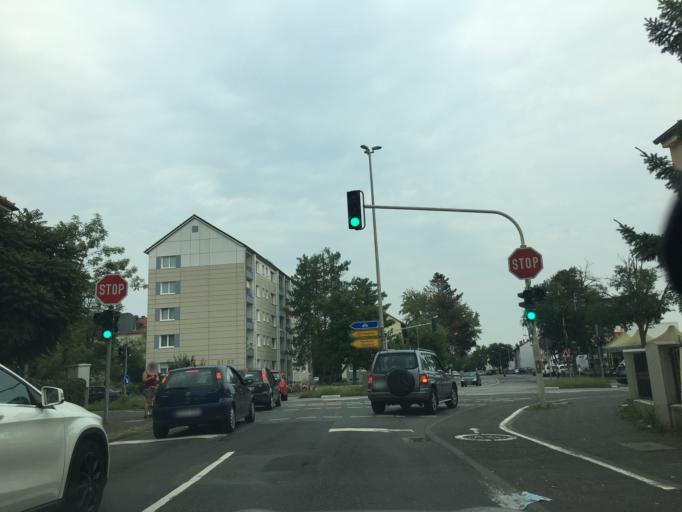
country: DE
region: Hesse
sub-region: Regierungsbezirk Darmstadt
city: Russelsheim
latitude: 49.9985
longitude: 8.4238
